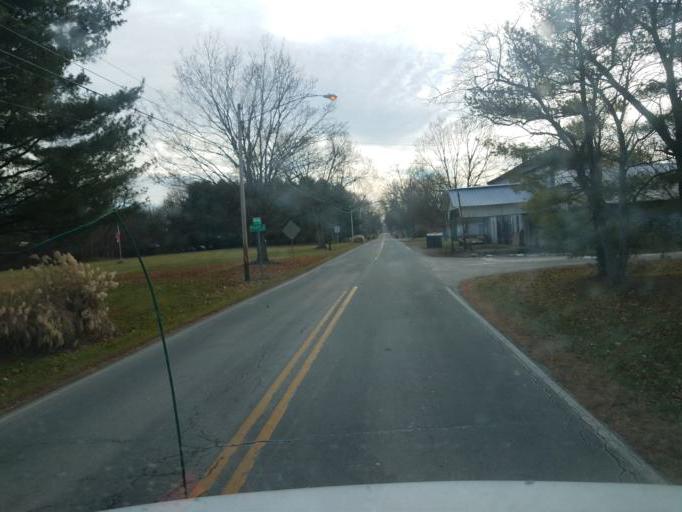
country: US
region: Ohio
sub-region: Delaware County
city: Ashley
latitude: 40.3294
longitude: -82.9573
